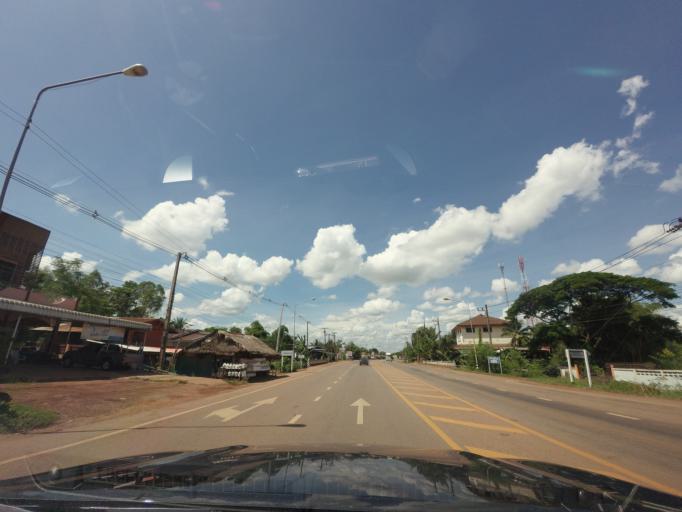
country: TH
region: Changwat Udon Thani
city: Ban Dung
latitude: 17.7091
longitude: 103.2506
